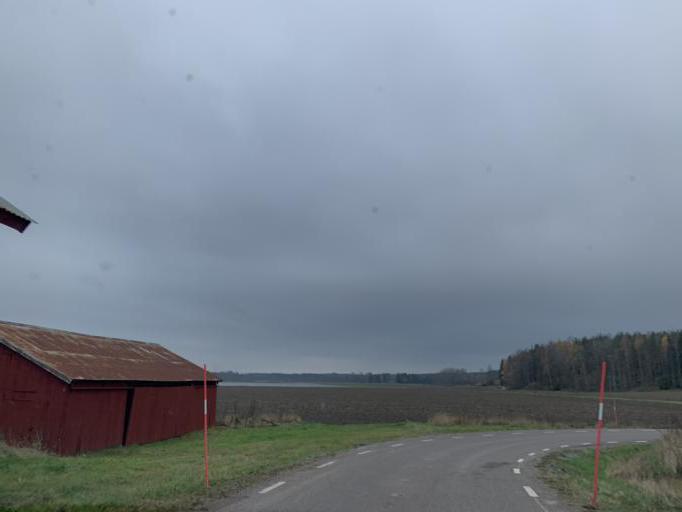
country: SE
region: Vaestmanland
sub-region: Surahammars Kommun
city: Ramnas
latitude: 59.7499
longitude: 16.1764
